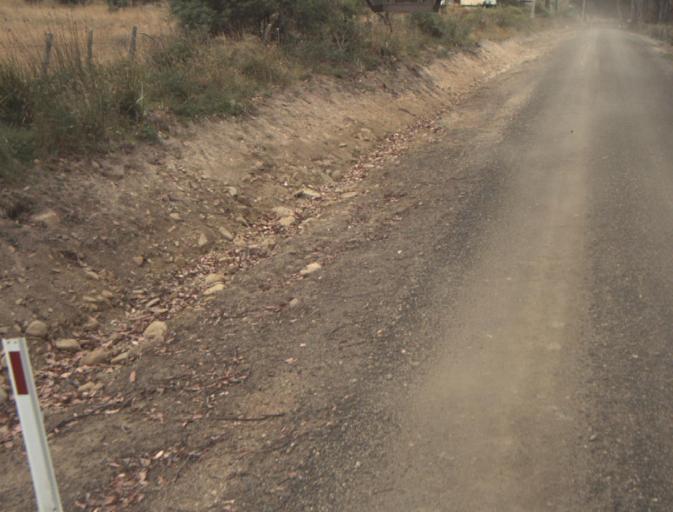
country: AU
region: Tasmania
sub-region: Northern Midlands
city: Evandale
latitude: -41.4576
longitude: 147.4460
